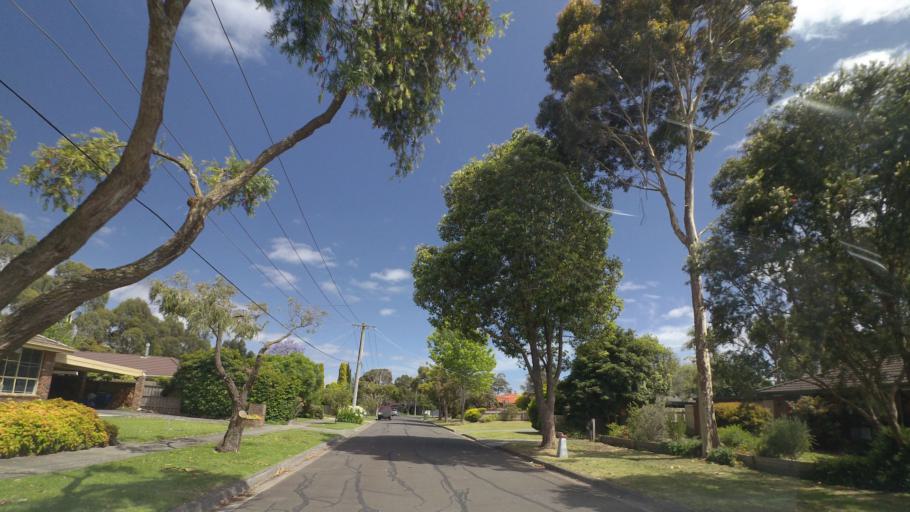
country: AU
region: Victoria
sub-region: Maroondah
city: Bayswater North
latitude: -37.8344
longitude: 145.2957
